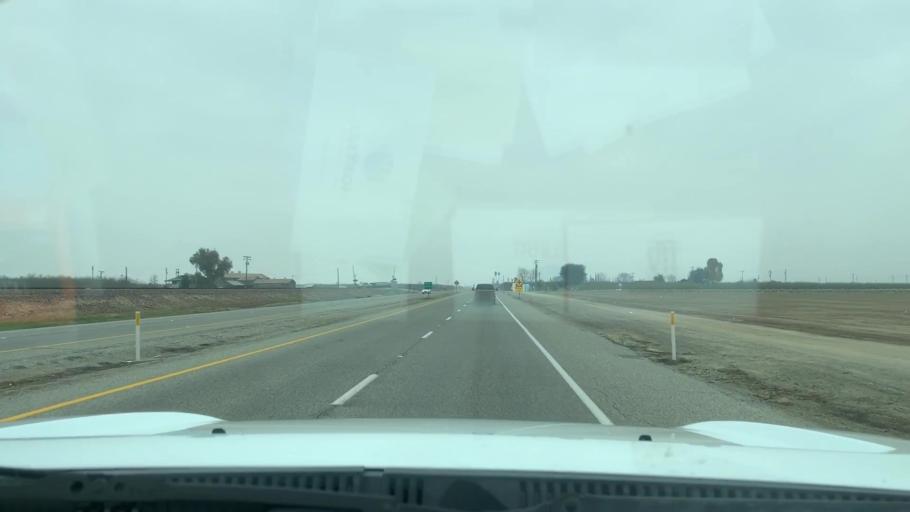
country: US
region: California
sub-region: Kern County
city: Shafter
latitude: 35.5225
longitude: -119.2982
